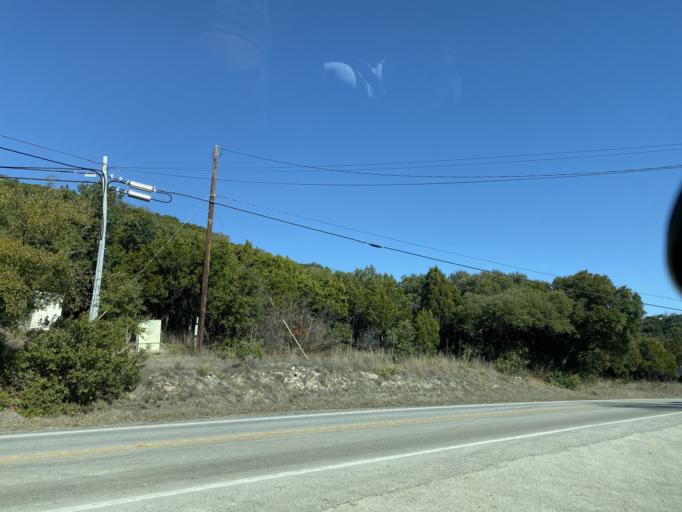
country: US
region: Texas
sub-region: Travis County
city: Hudson Bend
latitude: 30.4404
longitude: -97.8727
